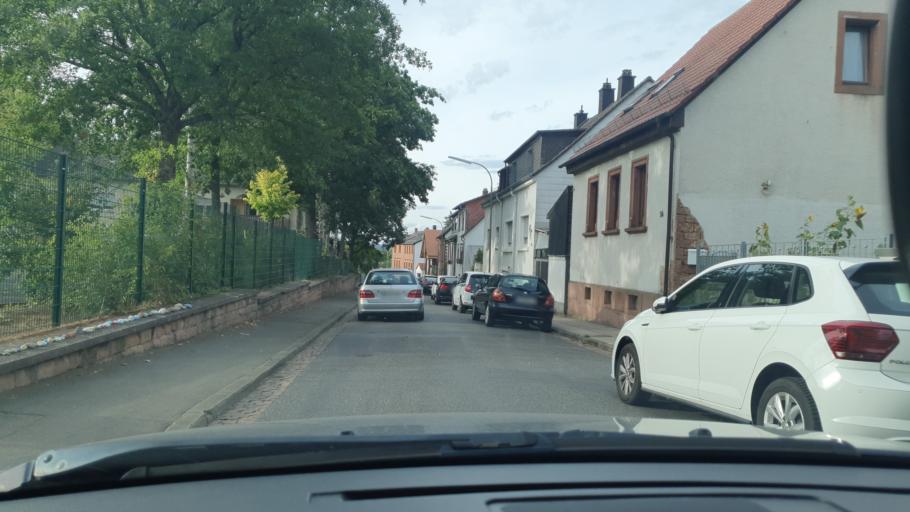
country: DE
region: Rheinland-Pfalz
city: Otterbach
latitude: 49.4705
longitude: 7.7658
